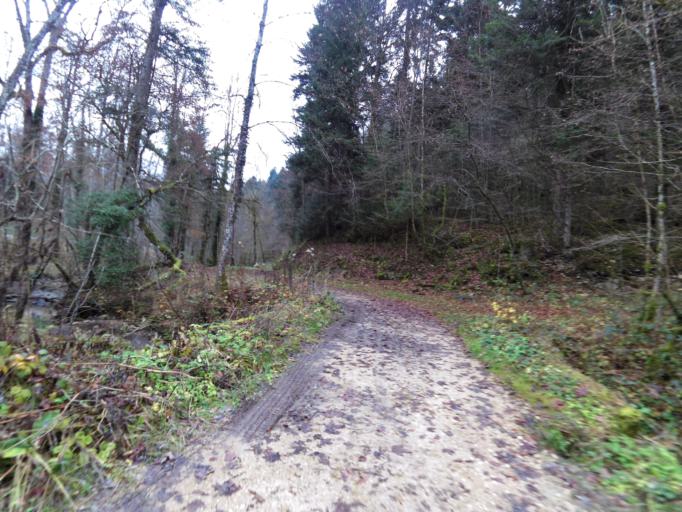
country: FR
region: Alsace
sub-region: Departement du Haut-Rhin
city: Ferrette
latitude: 47.4359
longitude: 7.2994
